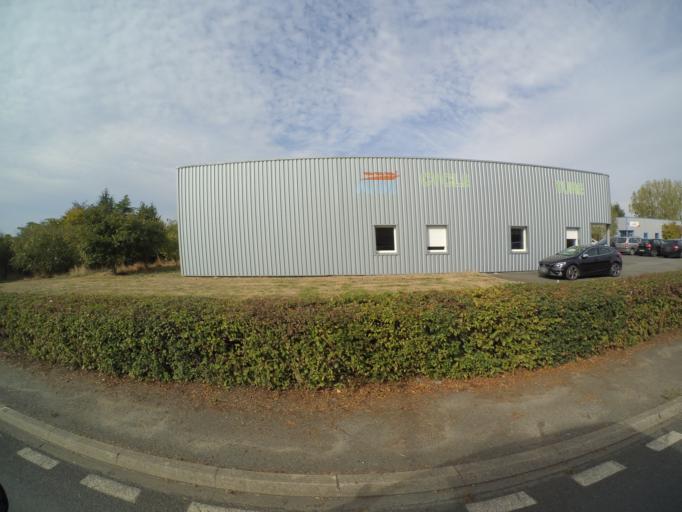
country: FR
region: Pays de la Loire
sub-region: Departement de Maine-et-Loire
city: Villedieu-la-Blouere
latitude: 47.1605
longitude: -1.0521
